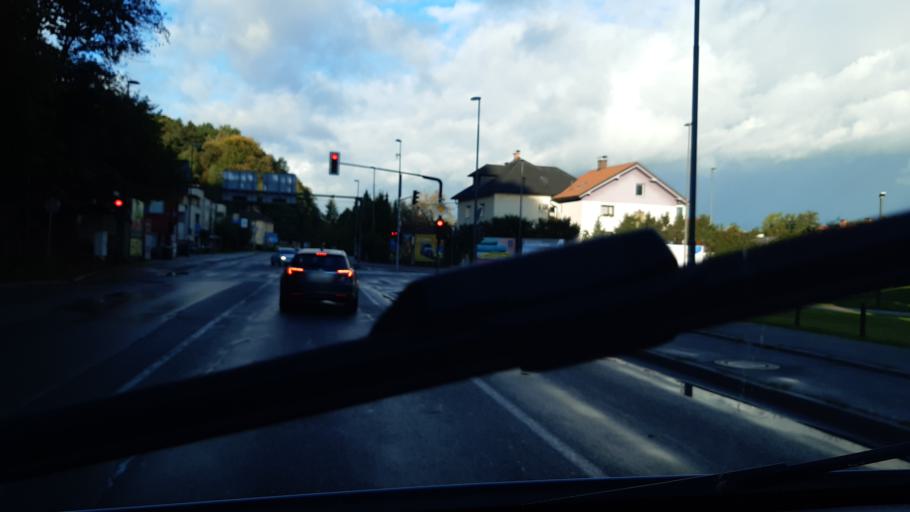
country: SI
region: Ljubljana
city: Ljubljana
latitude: 46.0481
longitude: 14.5392
